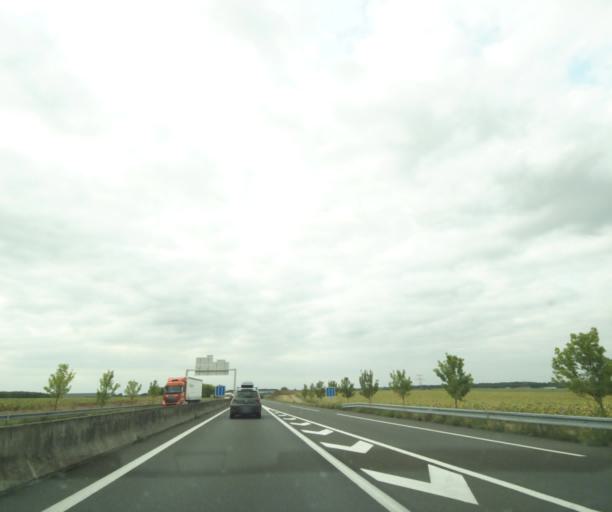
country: FR
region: Centre
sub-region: Departement d'Indre-et-Loire
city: Parcay-Meslay
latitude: 47.4672
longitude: 0.7622
